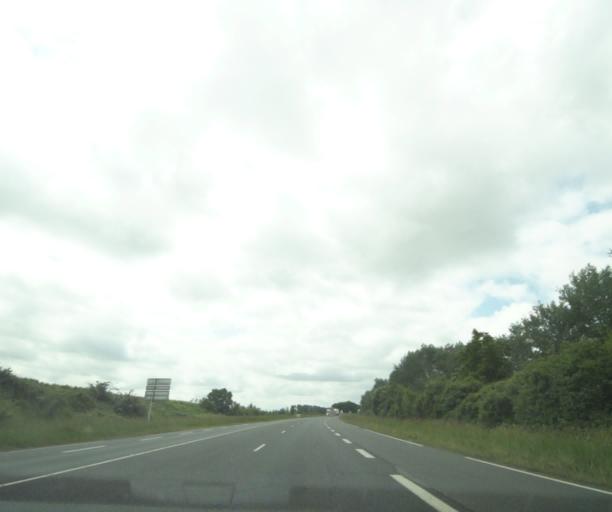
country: FR
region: Poitou-Charentes
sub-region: Departement des Deux-Sevres
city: Airvault
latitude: 46.8241
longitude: -0.2042
